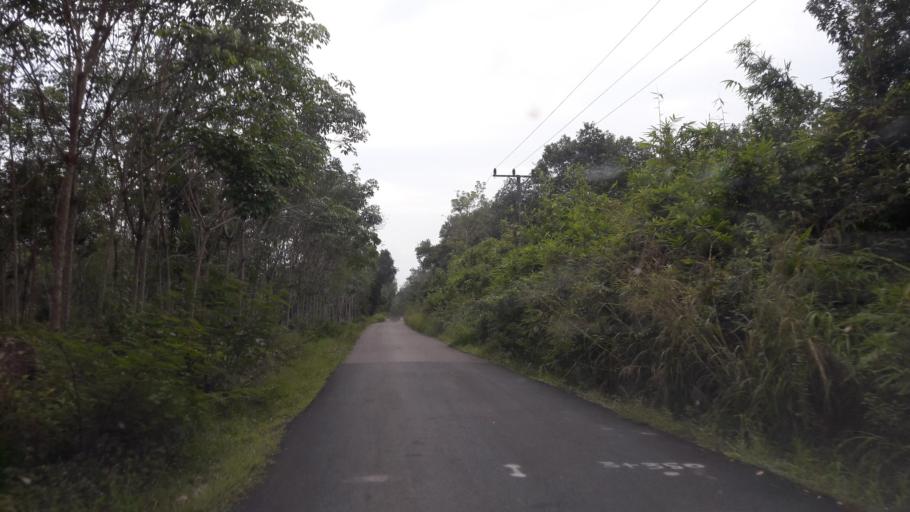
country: ID
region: South Sumatra
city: Gunungmenang
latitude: -3.1239
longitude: 104.1034
